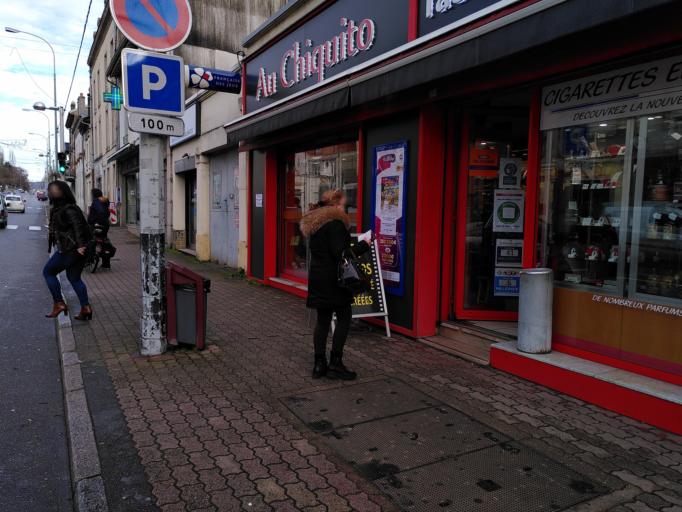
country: FR
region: Lorraine
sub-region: Departement de Meurthe-et-Moselle
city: Pompey
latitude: 48.7684
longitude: 6.1285
